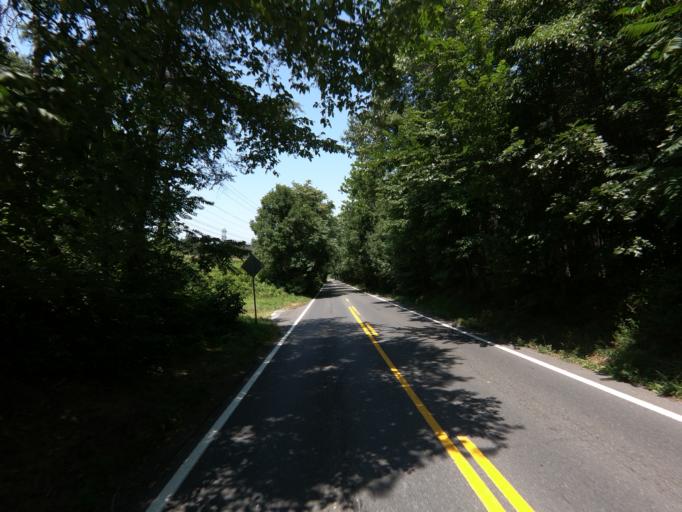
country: US
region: Maryland
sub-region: Frederick County
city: Green Valley
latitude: 39.2747
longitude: -77.3106
